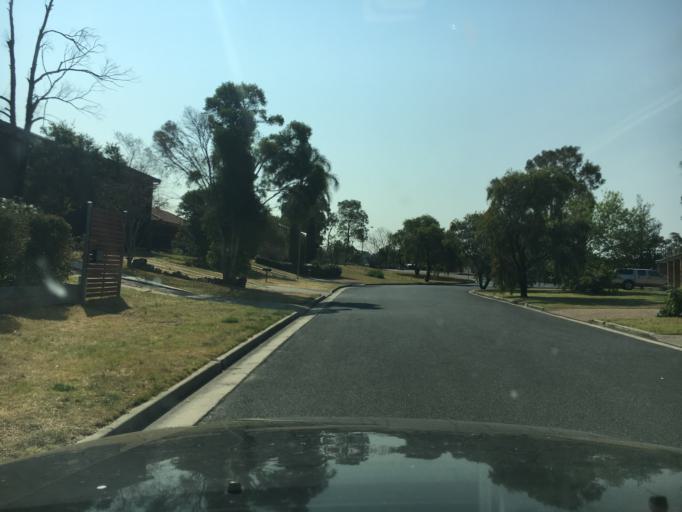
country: AU
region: New South Wales
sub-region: Singleton
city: Singleton
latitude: -32.5582
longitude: 151.1584
